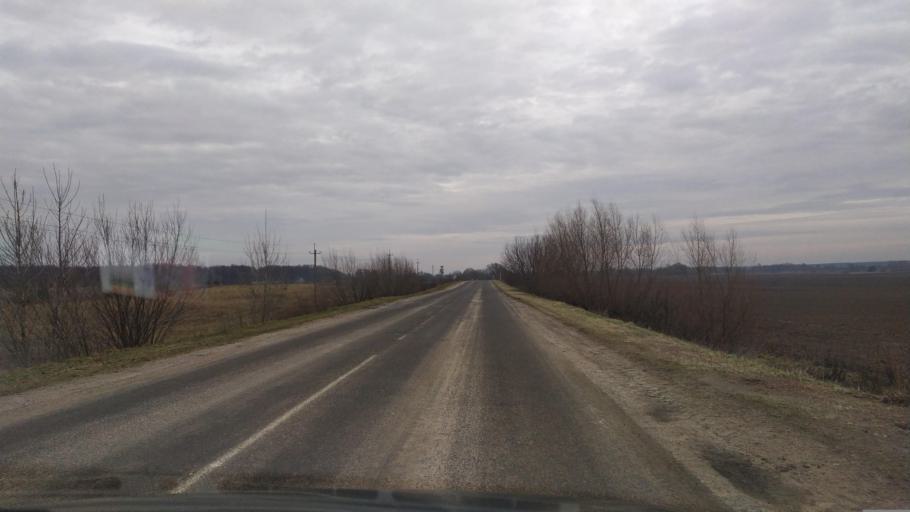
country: BY
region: Brest
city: Kamyanyets
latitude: 52.4335
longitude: 23.8340
